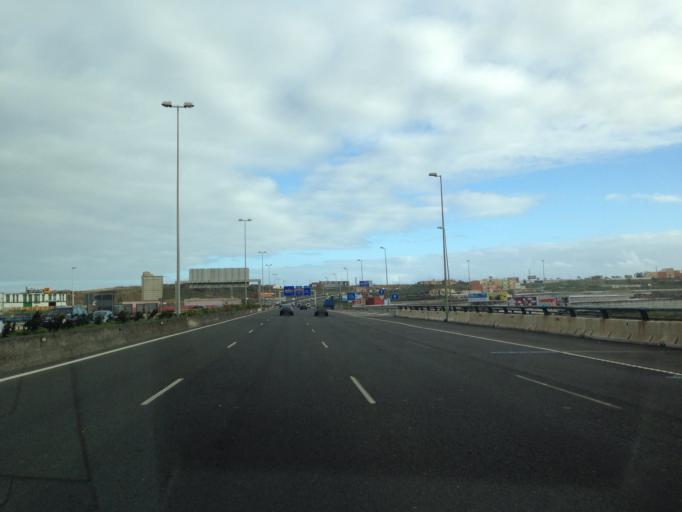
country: ES
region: Canary Islands
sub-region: Provincia de Las Palmas
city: Telde
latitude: 28.0253
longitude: -15.3924
